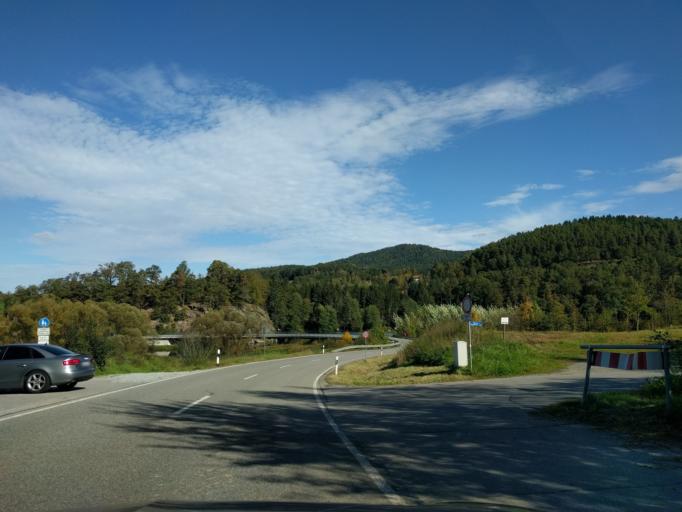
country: DE
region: Bavaria
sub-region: Lower Bavaria
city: Viechtach
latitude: 49.0906
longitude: 12.8871
